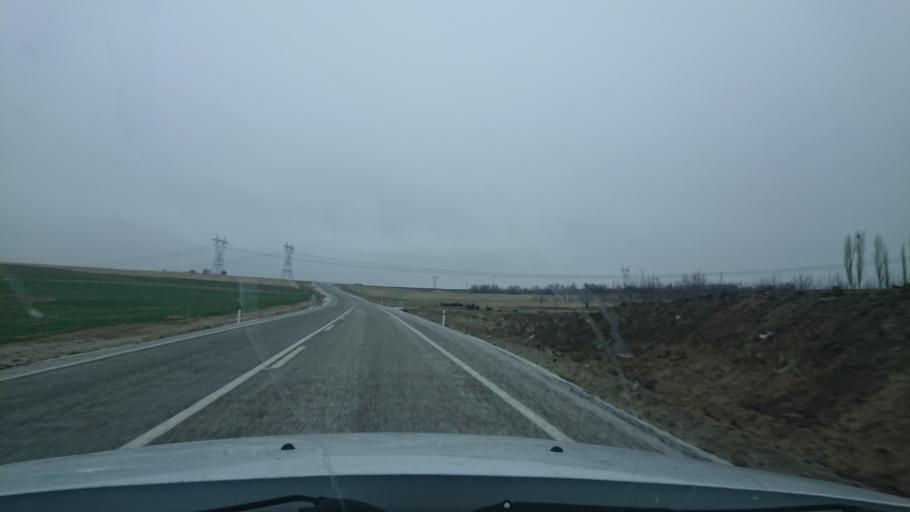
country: TR
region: Aksaray
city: Agacoren
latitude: 38.9018
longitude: 33.9334
